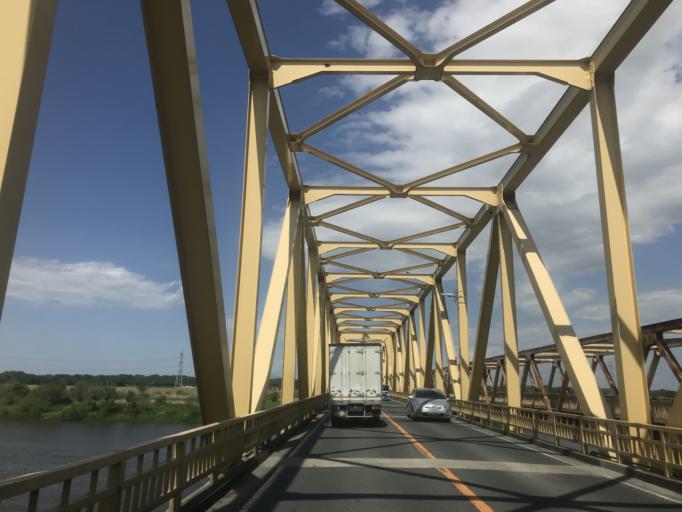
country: JP
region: Chiba
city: Noda
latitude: 35.9828
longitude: 139.8904
